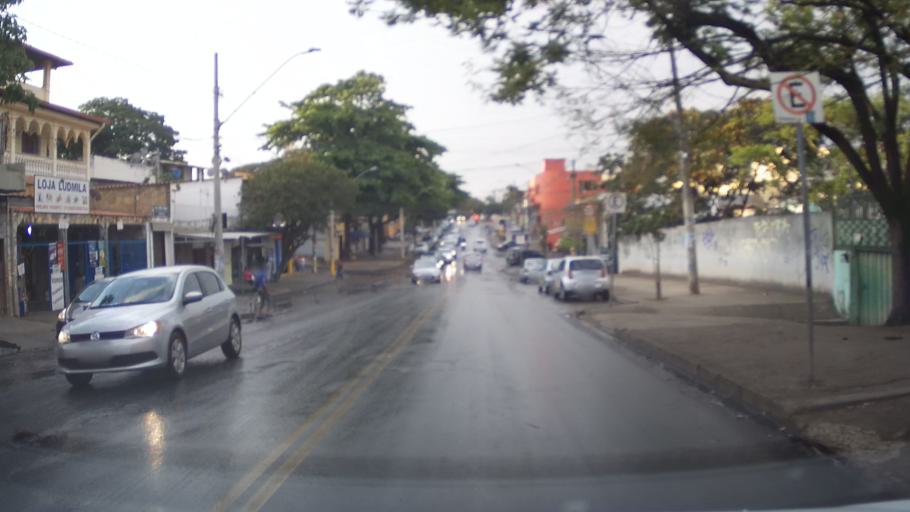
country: BR
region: Minas Gerais
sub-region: Belo Horizonte
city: Belo Horizonte
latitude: -19.9679
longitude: -43.9813
